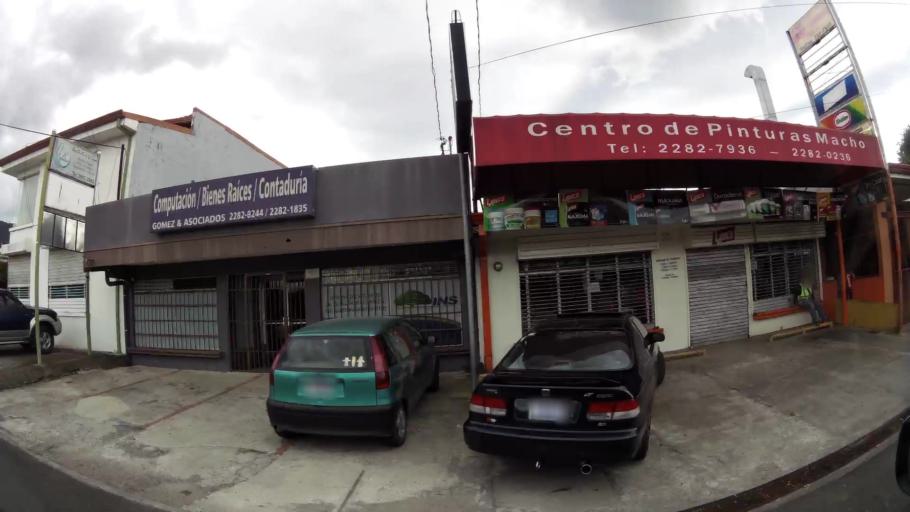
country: CR
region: San Jose
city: Santa Ana
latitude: 9.9322
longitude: -84.1832
